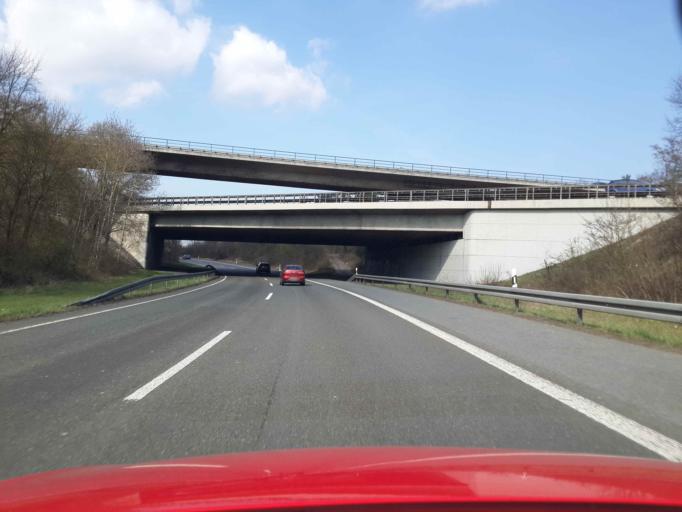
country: DE
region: Hesse
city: Raunheim
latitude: 50.0260
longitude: 8.4932
